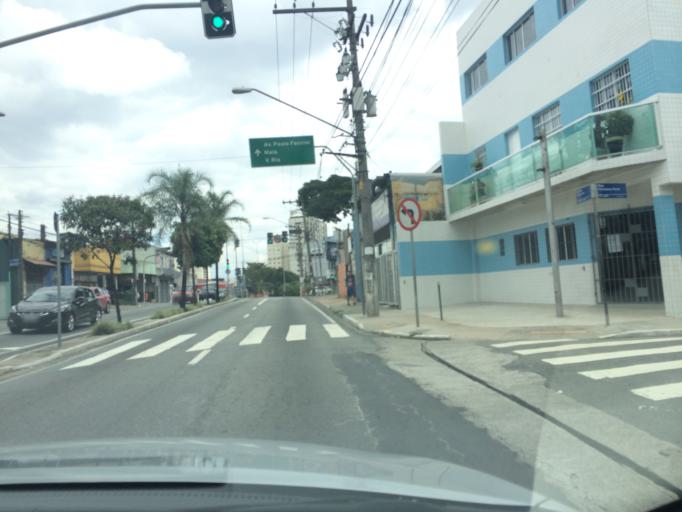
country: BR
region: Sao Paulo
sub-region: Guarulhos
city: Guarulhos
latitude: -23.4608
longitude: -46.5234
